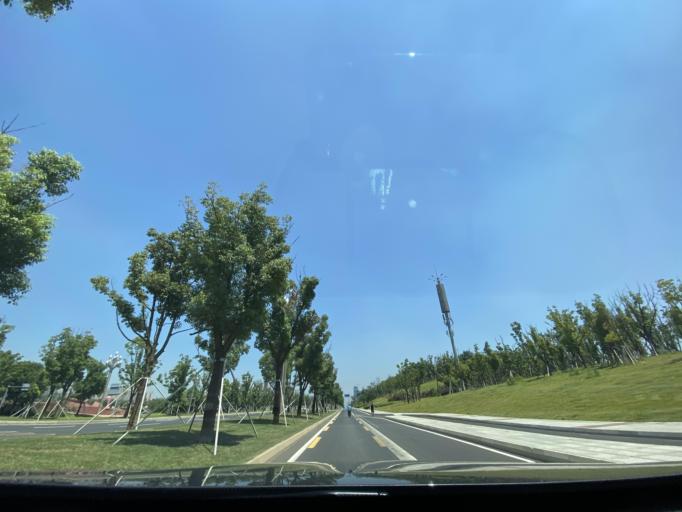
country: CN
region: Sichuan
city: Dongsheng
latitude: 30.4686
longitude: 104.0695
